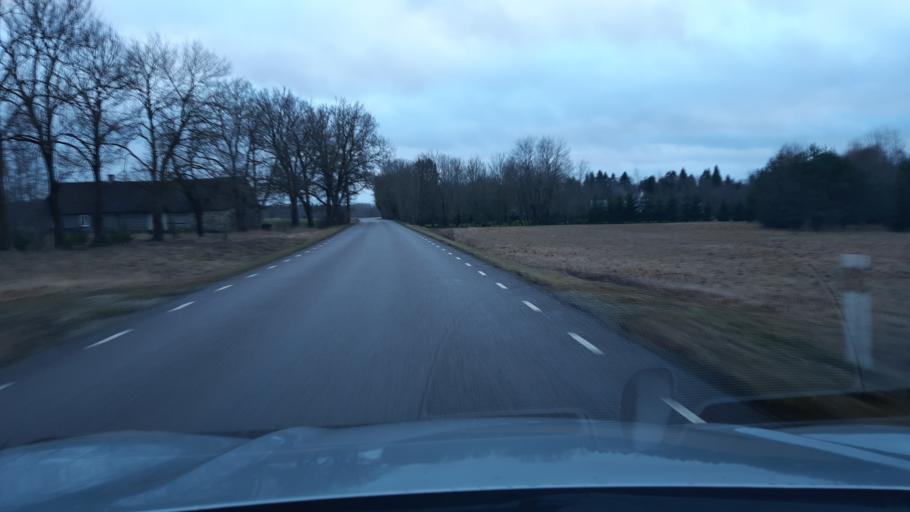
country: EE
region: Raplamaa
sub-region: Kohila vald
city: Kohila
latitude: 59.1521
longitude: 24.6526
